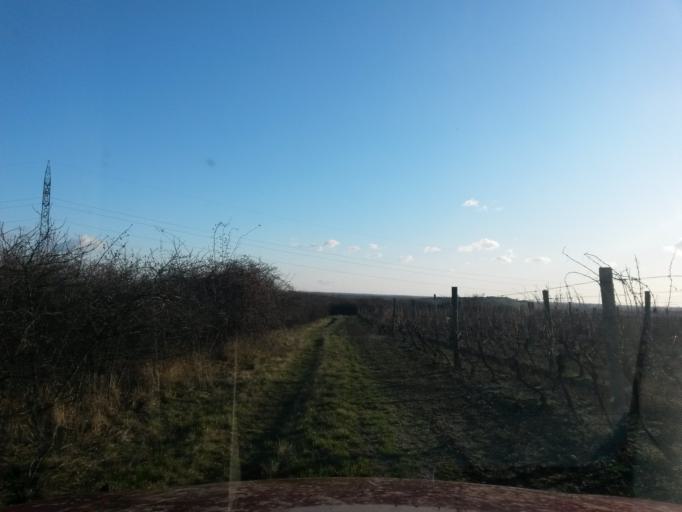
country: HU
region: Borsod-Abauj-Zemplen
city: Sarospatak
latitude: 48.3243
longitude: 21.5379
